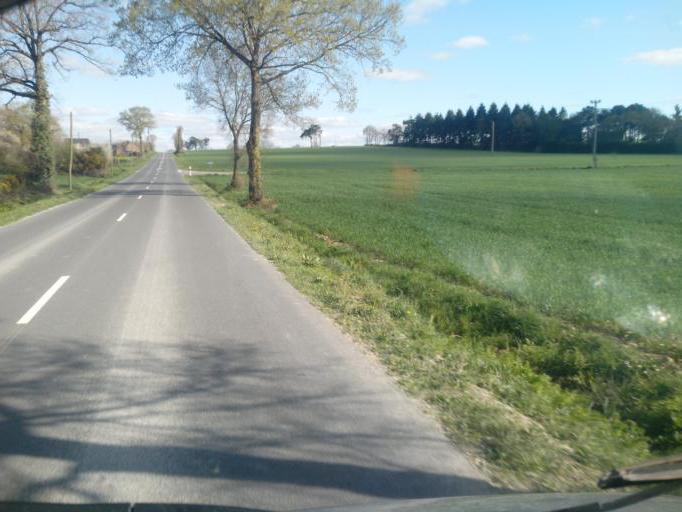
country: FR
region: Brittany
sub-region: Departement d'Ille-et-Vilaine
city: Maure-de-Bretagne
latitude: 47.8776
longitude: -1.9240
